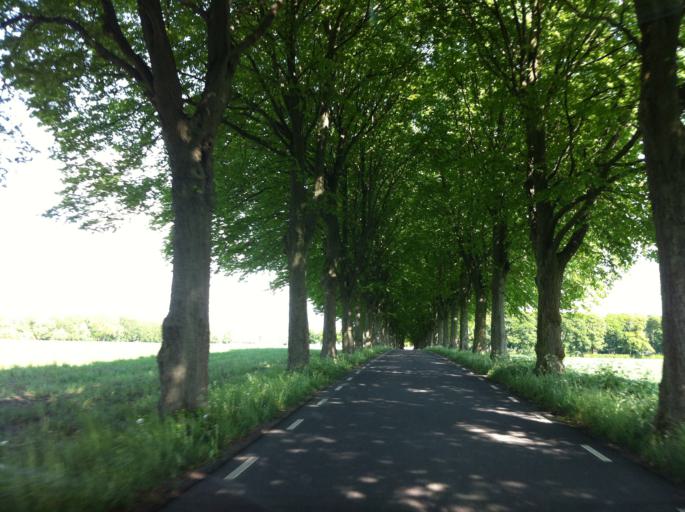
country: SE
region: Skane
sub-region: Helsingborg
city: Glumslov
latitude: 55.9638
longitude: 12.8981
